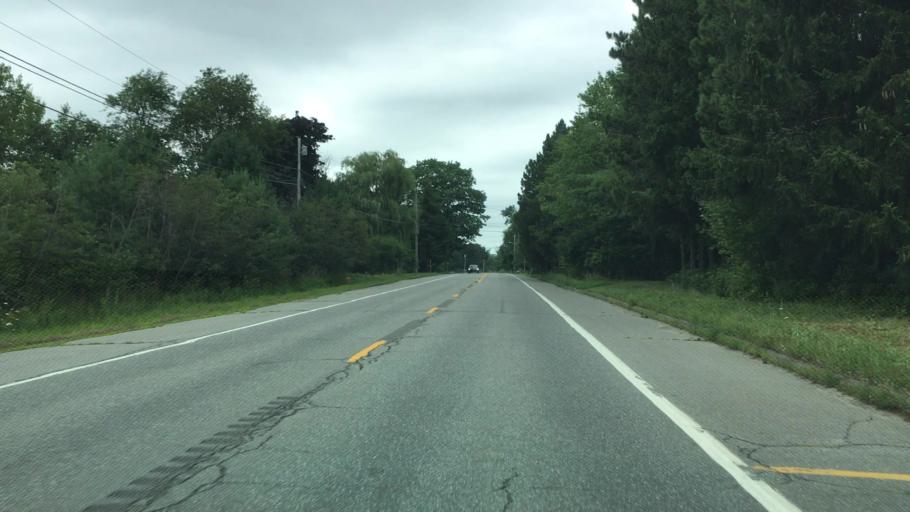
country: US
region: Maine
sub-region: Waldo County
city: Winterport
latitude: 44.6846
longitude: -68.8451
